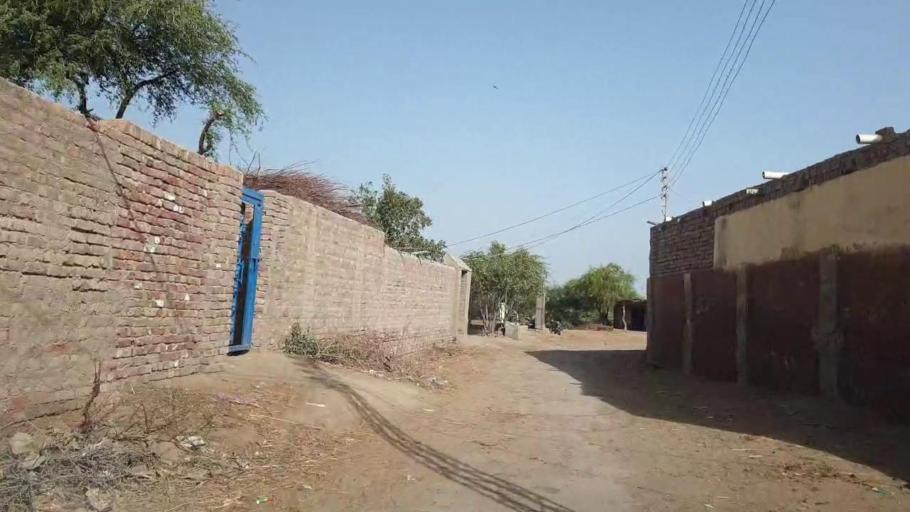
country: PK
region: Sindh
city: Tando Ghulam Ali
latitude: 25.0701
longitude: 68.8618
